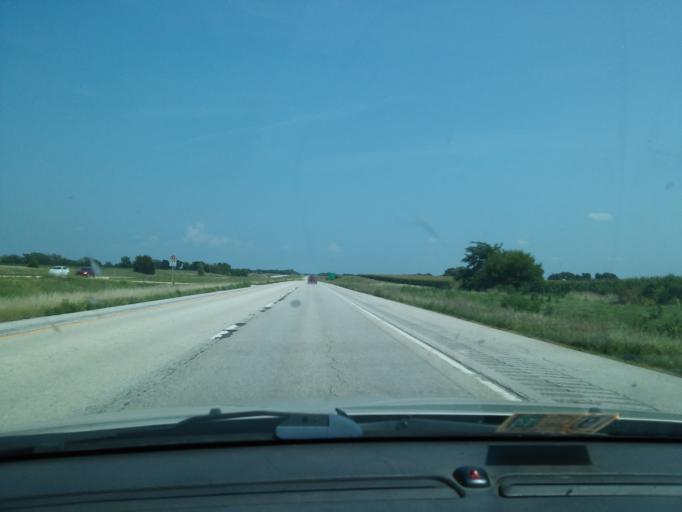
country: US
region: Illinois
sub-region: Sangamon County
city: New Berlin
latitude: 39.7367
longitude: -90.0622
